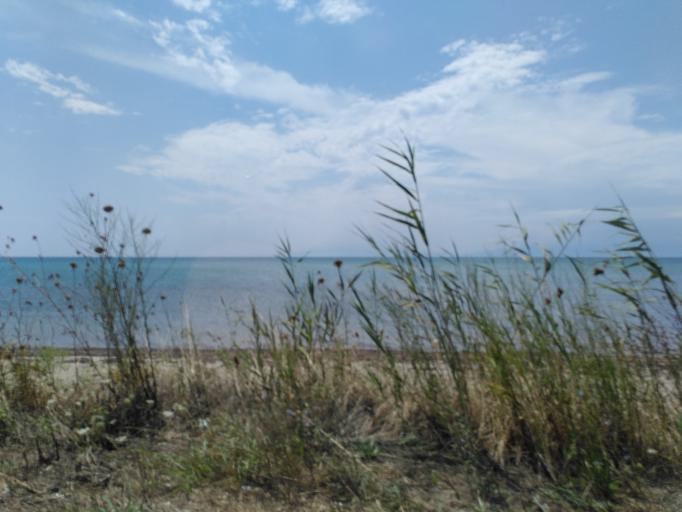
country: GR
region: Central Macedonia
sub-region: Nomos Thessalonikis
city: Nea Michaniona
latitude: 40.4296
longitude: 22.8745
